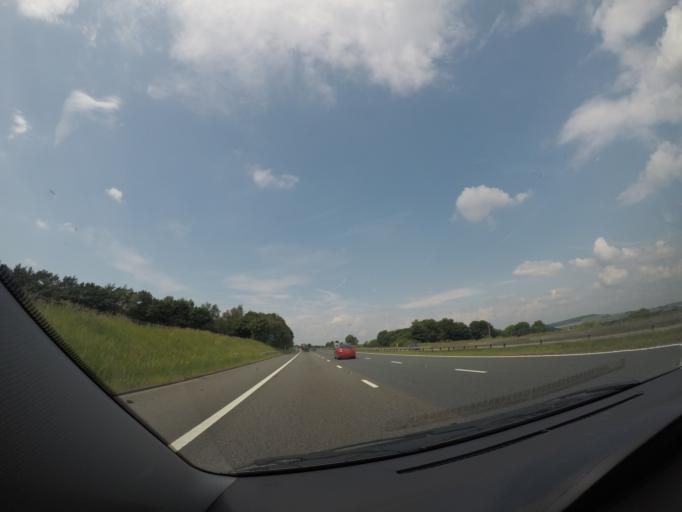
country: GB
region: England
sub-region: Cumbria
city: Scotby
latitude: 54.7811
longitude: -2.8558
